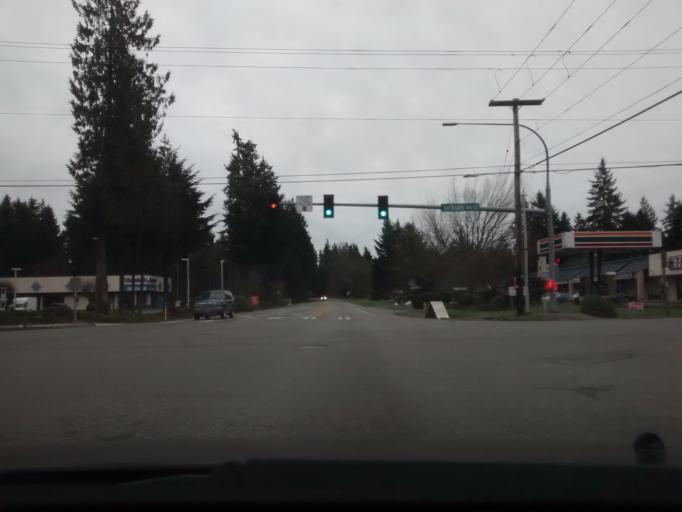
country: US
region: Washington
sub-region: Kitsap County
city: Parkwood
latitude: 47.5194
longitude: -122.6100
